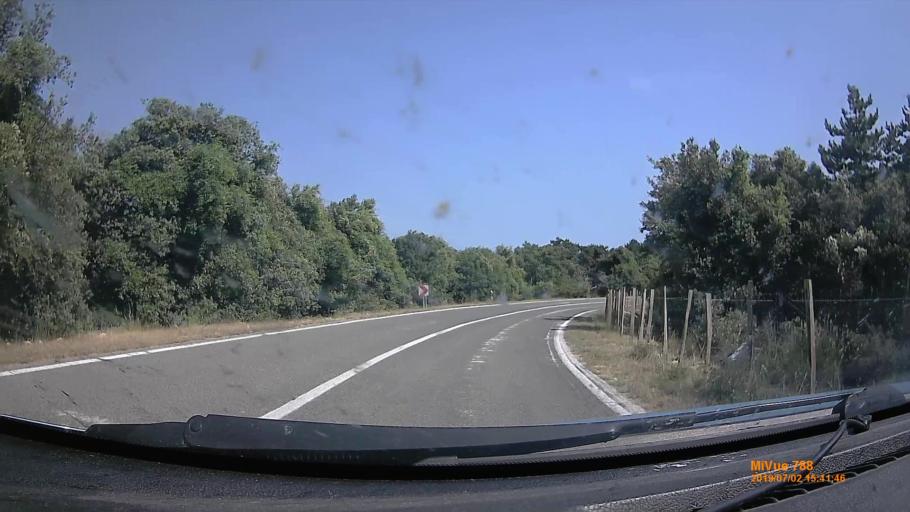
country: HR
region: Primorsko-Goranska
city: Cres
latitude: 44.9609
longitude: 14.4465
